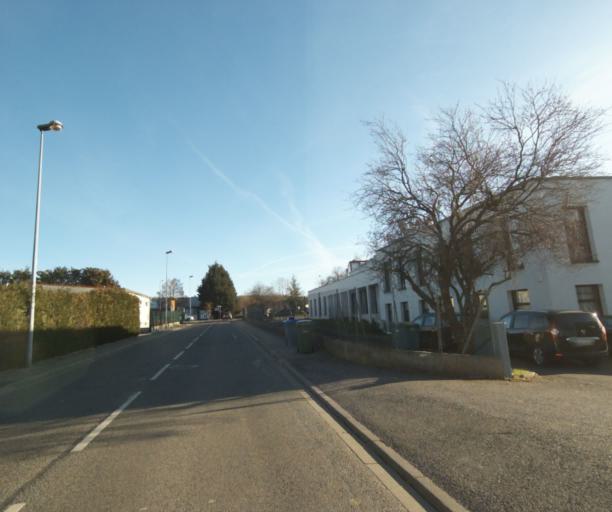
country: FR
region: Lorraine
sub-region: Departement de Meurthe-et-Moselle
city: Pulnoy
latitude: 48.7053
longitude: 6.2550
